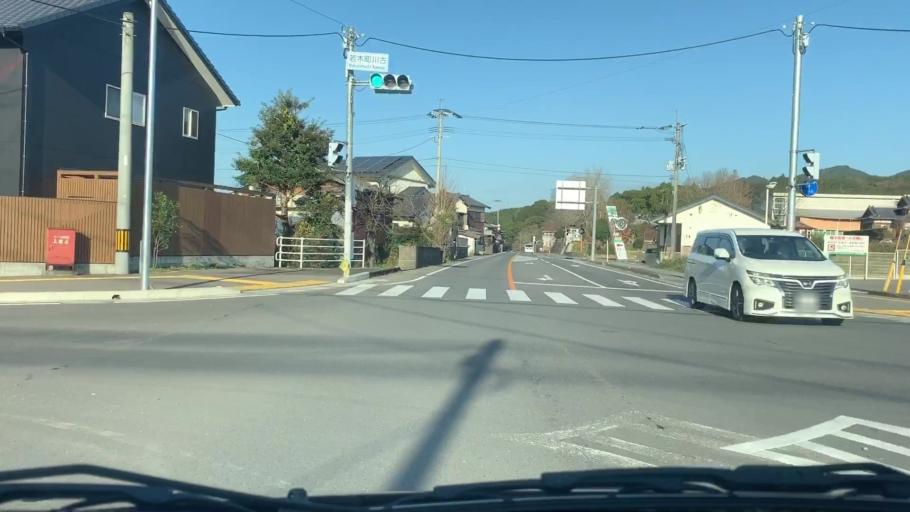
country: JP
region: Saga Prefecture
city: Takeocho-takeo
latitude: 33.2515
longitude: 129.9956
